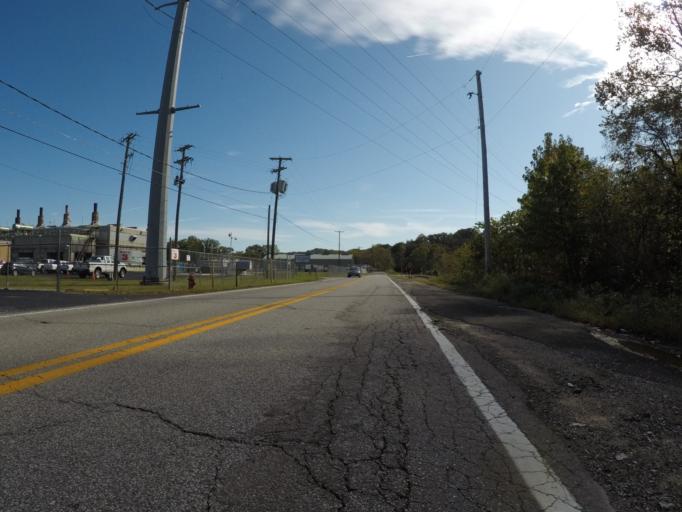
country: US
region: West Virginia
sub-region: Wayne County
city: Ceredo
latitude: 38.3670
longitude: -82.5333
